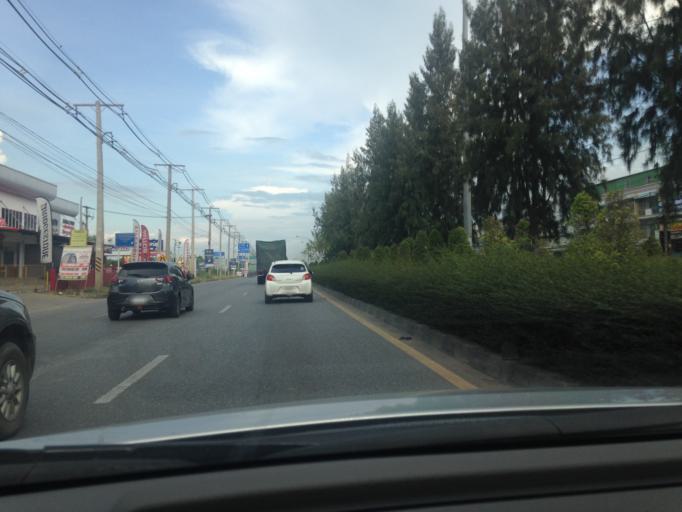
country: TH
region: Pathum Thani
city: Khlong Luang
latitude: 14.0669
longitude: 100.6916
